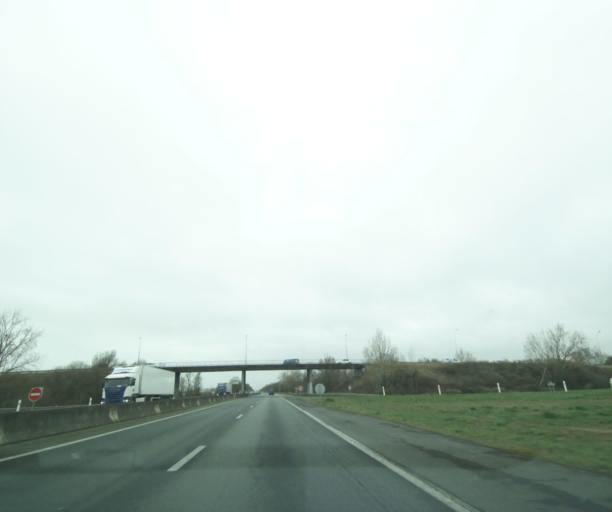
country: FR
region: Poitou-Charentes
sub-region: Departement de la Charente-Maritime
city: Chatelaillon-Plage
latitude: 46.0818
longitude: -1.0774
